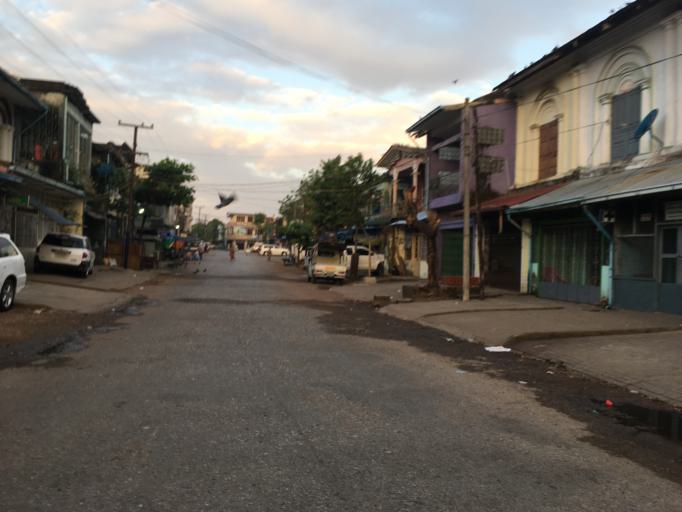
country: MM
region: Mon
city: Mawlamyine
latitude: 16.4857
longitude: 97.6236
